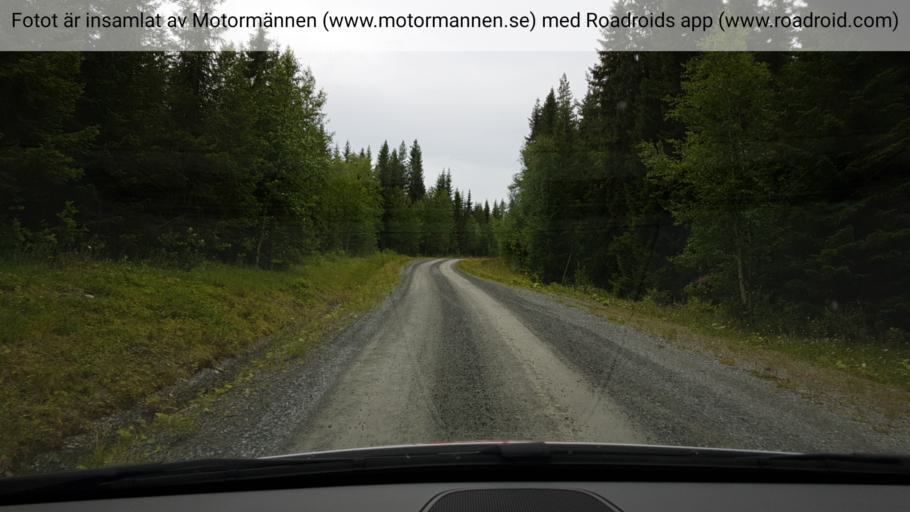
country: SE
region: Jaemtland
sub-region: Krokoms Kommun
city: Valla
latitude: 63.5824
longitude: 13.9569
